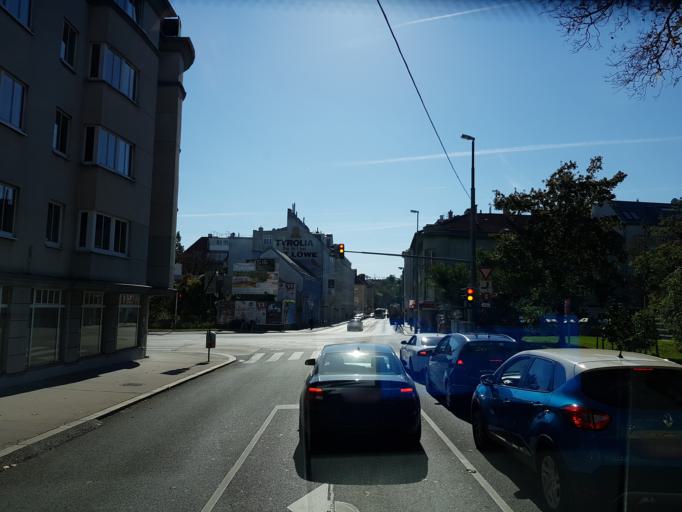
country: AT
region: Vienna
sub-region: Wien Stadt
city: Vienna
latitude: 48.2457
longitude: 16.3496
